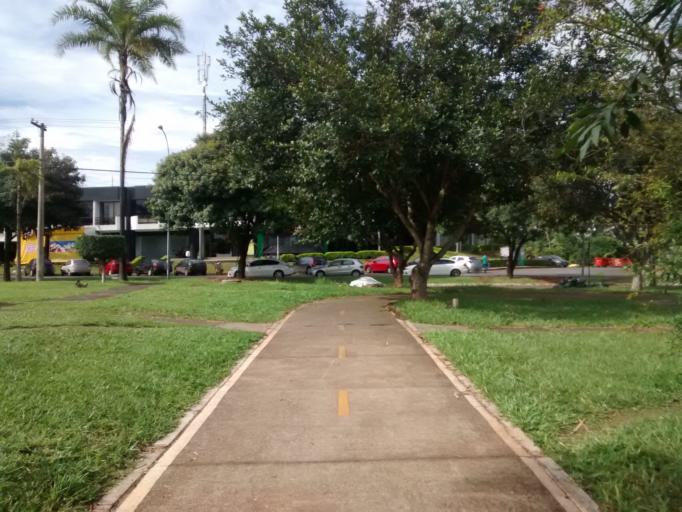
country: BR
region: Federal District
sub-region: Brasilia
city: Brasilia
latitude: -15.7979
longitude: -47.9189
